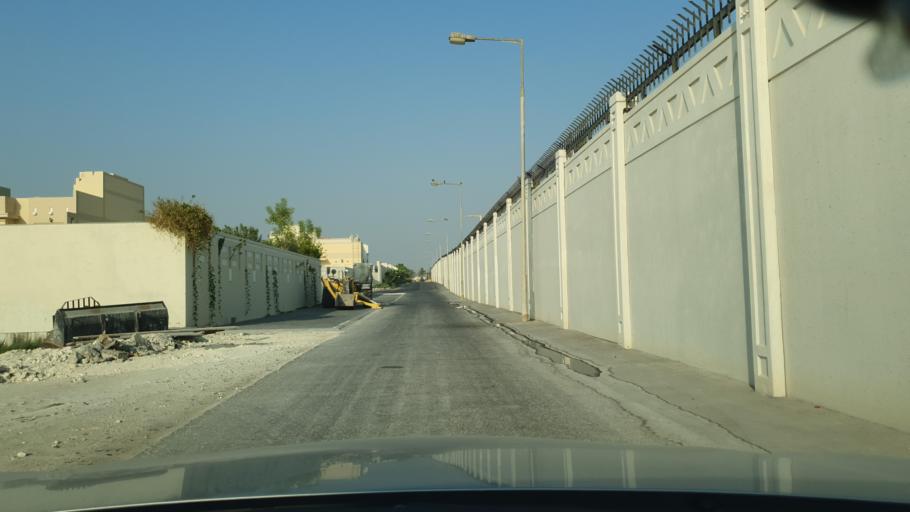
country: BH
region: Northern
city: Madinat `Isa
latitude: 26.1547
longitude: 50.5400
